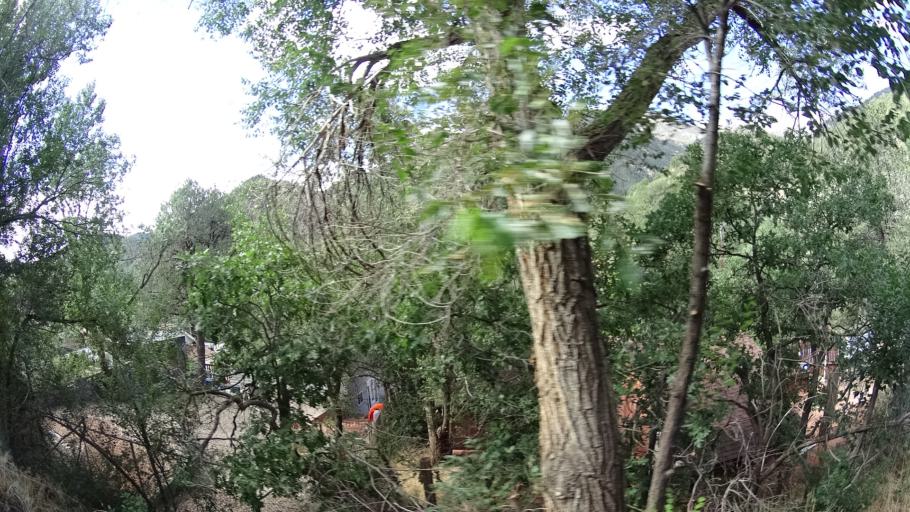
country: US
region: Colorado
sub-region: El Paso County
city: Manitou Springs
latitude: 38.8610
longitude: -104.9246
